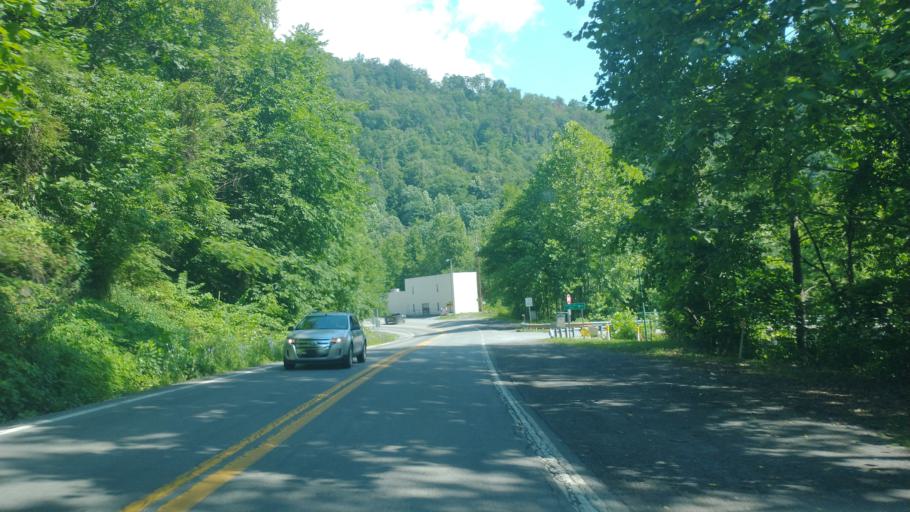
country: US
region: West Virginia
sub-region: McDowell County
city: Welch
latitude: 37.4292
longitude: -81.5523
